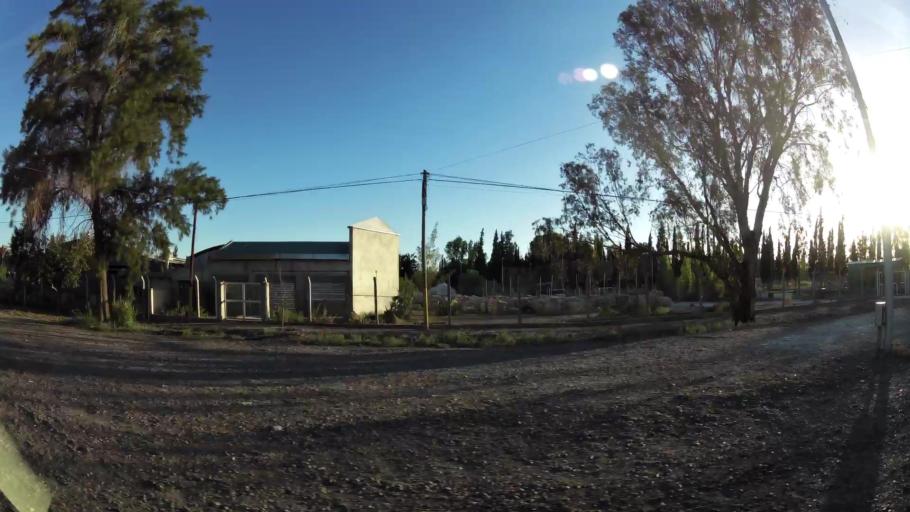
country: AR
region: San Juan
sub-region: Departamento de Santa Lucia
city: Santa Lucia
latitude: -31.5484
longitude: -68.4849
